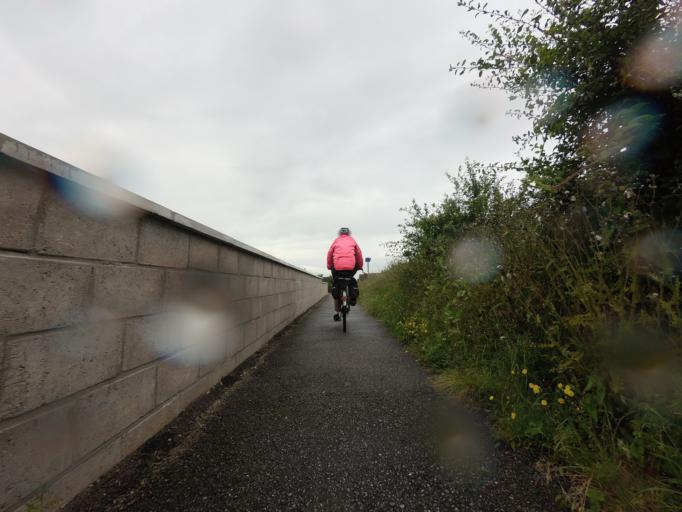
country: GB
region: Scotland
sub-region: Moray
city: Buckie
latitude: 57.6829
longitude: -2.9394
